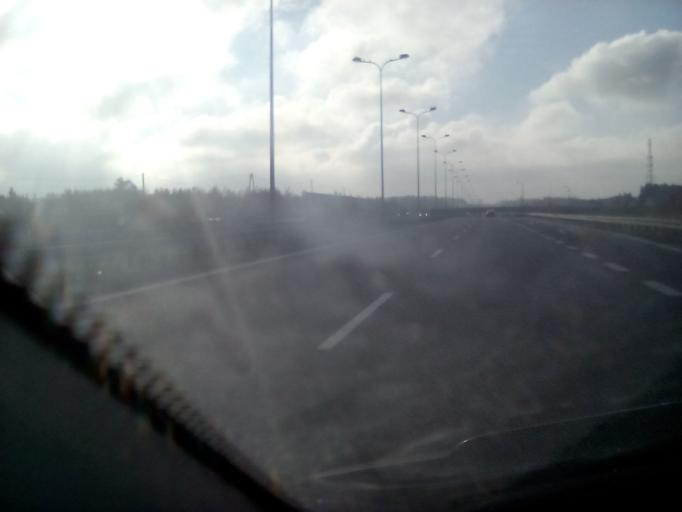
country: PL
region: Masovian Voivodeship
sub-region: Powiat grojecki
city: Goszczyn
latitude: 51.7391
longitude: 20.9131
